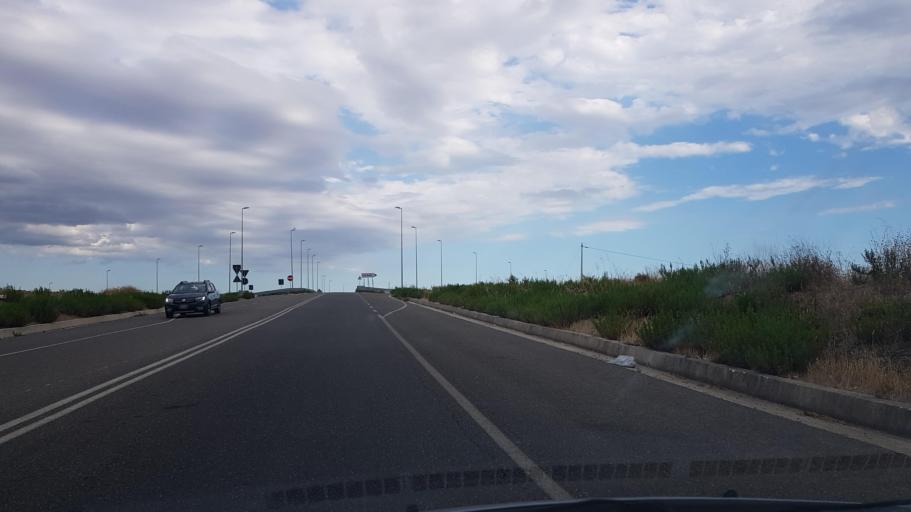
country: IT
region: Apulia
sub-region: Provincia di Taranto
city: Taranto
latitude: 40.4462
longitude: 17.2799
